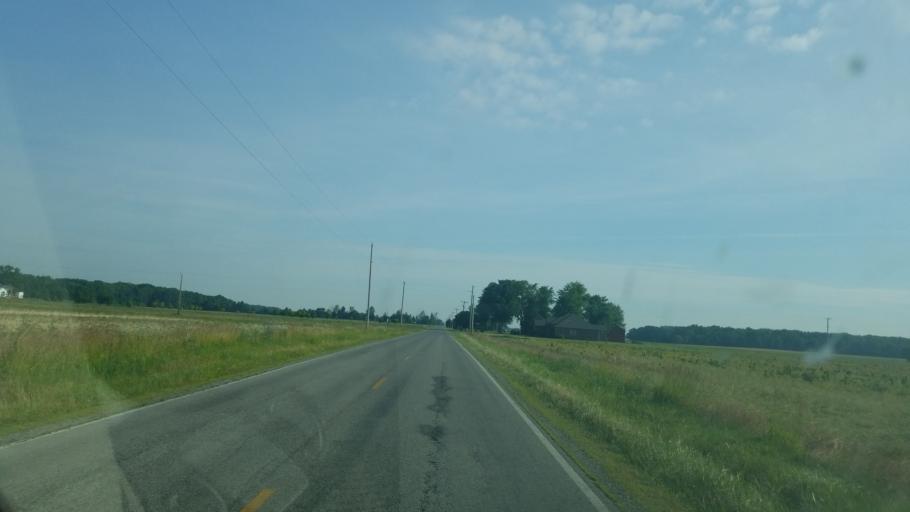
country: US
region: Ohio
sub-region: Hancock County
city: Arlington
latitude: 40.9347
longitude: -83.6986
